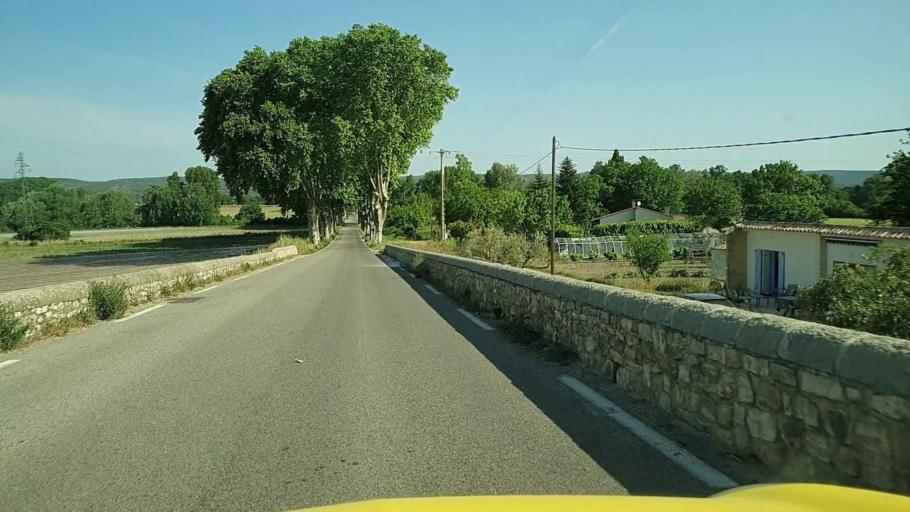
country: FR
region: Languedoc-Roussillon
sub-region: Departement du Gard
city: Uzes
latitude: 44.0306
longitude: 4.4111
